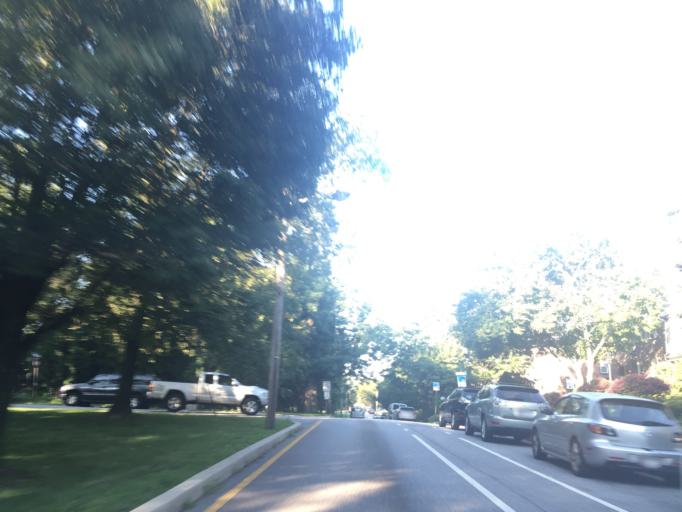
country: US
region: Maryland
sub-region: Baltimore County
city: Charlestown
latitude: 39.2905
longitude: -76.7064
